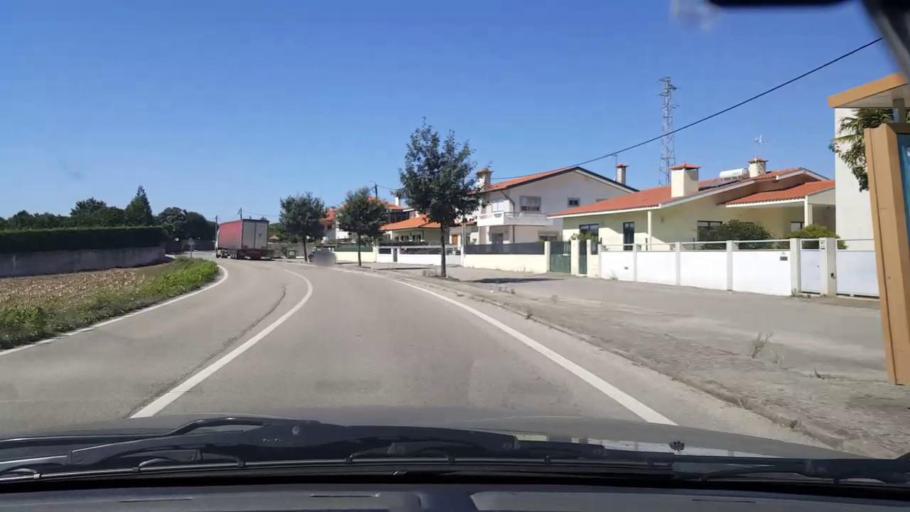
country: PT
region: Porto
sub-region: Vila do Conde
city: Arvore
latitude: 41.3408
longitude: -8.6958
